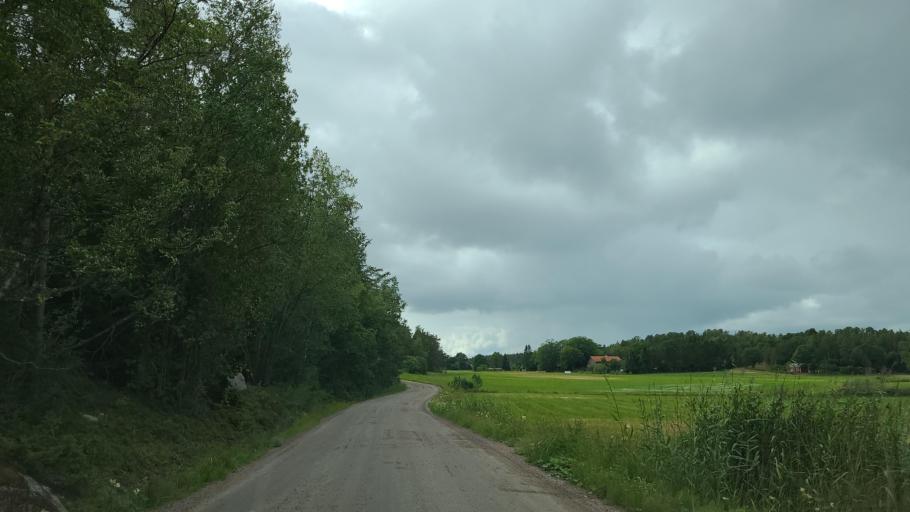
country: FI
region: Varsinais-Suomi
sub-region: Aboland-Turunmaa
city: Nagu
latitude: 60.2010
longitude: 21.8898
